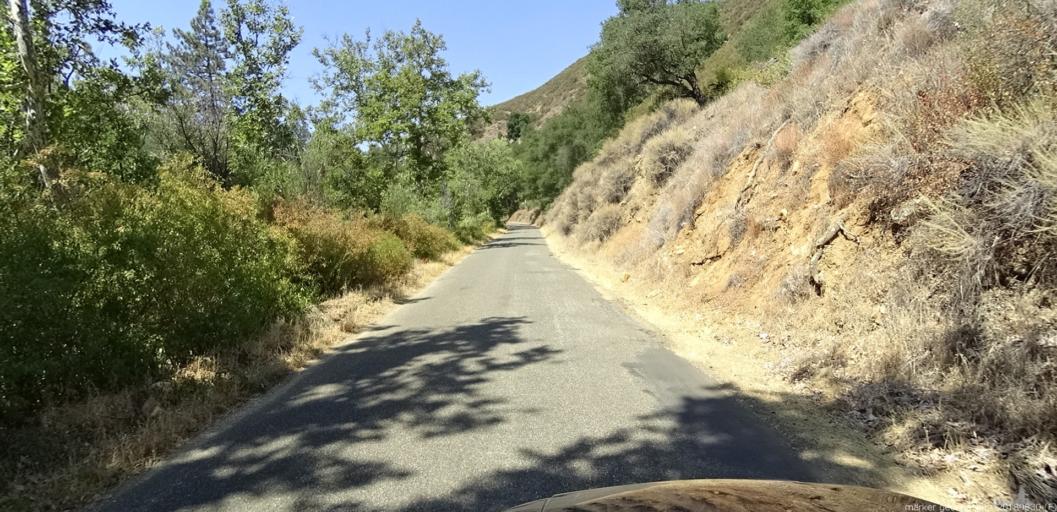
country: US
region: California
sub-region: Monterey County
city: King City
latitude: 35.9956
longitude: -121.3704
